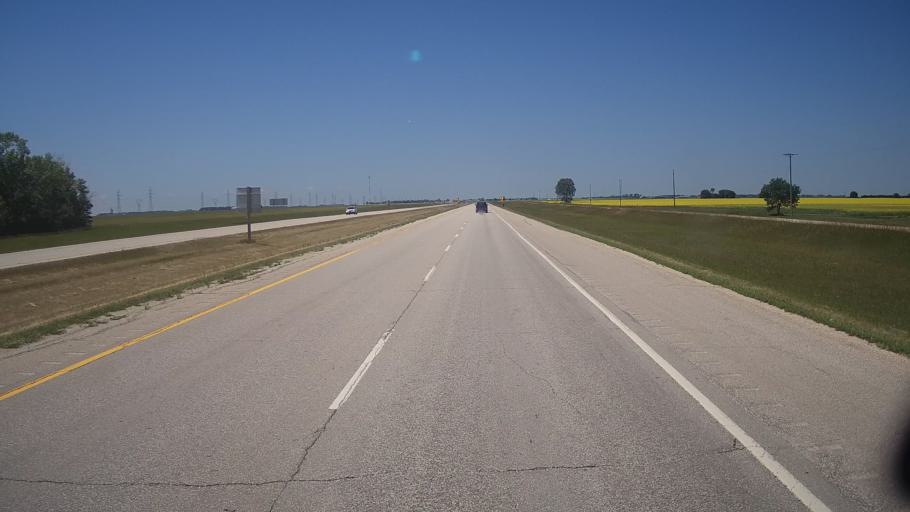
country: CA
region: Manitoba
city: Stonewall
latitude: 49.9900
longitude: -97.2761
